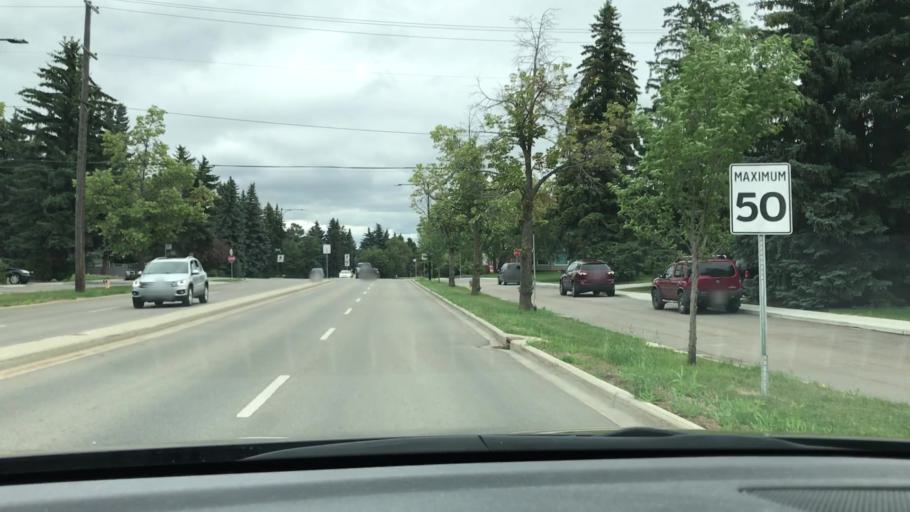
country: CA
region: Alberta
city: Edmonton
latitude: 53.5193
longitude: -113.5640
